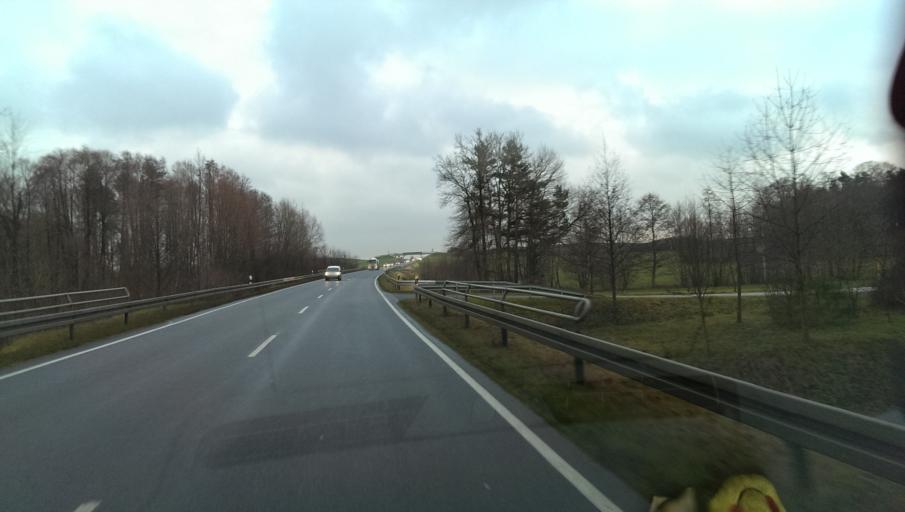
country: DE
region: Saxony
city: Moritzburg
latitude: 51.1489
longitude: 13.6477
